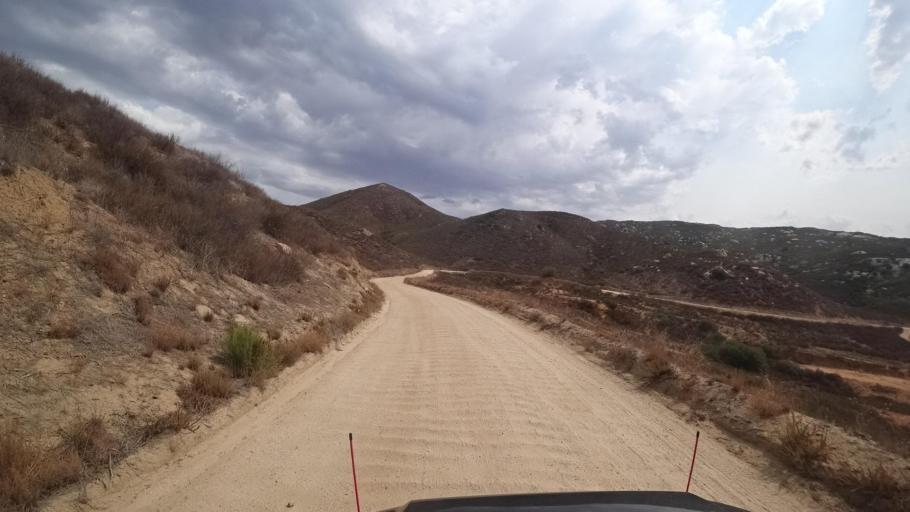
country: US
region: California
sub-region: San Diego County
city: Ramona
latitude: 33.1071
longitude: -116.8256
